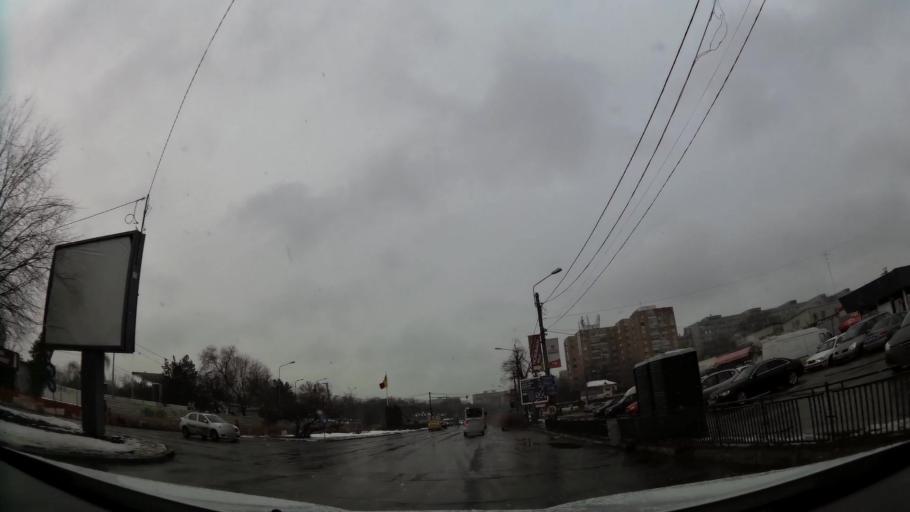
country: RO
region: Ilfov
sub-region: Comuna Chiajna
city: Rosu
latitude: 44.4225
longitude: 26.0359
